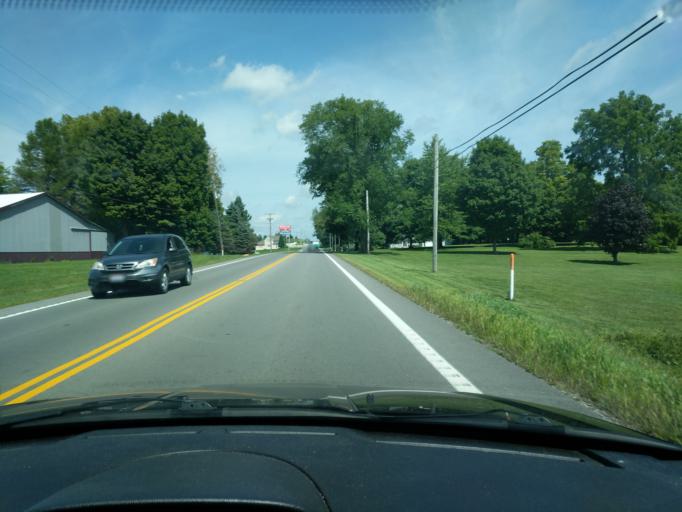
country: US
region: Ohio
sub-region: Logan County
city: West Liberty
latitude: 40.3014
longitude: -83.7592
